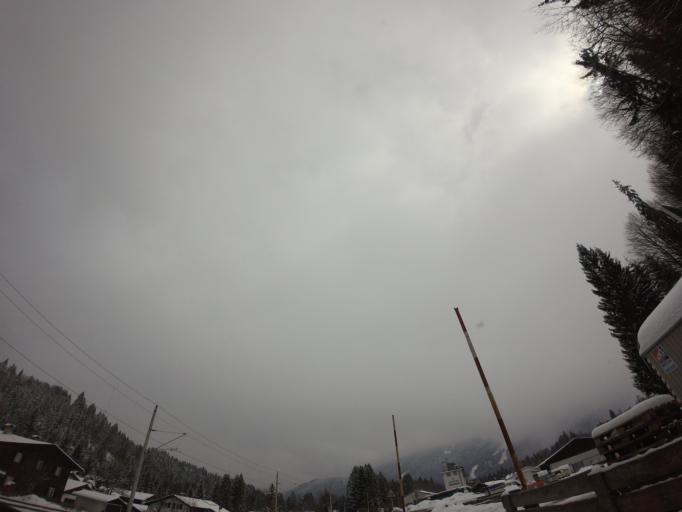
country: DE
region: Bavaria
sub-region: Upper Bavaria
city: Grainau
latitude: 47.4832
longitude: 11.0390
